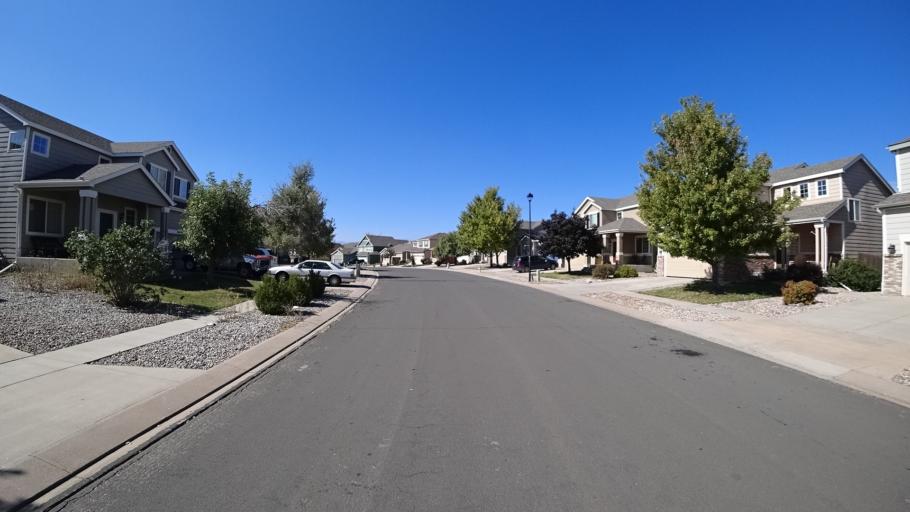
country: US
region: Colorado
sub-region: El Paso County
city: Cimarron Hills
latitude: 38.8973
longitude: -104.6945
